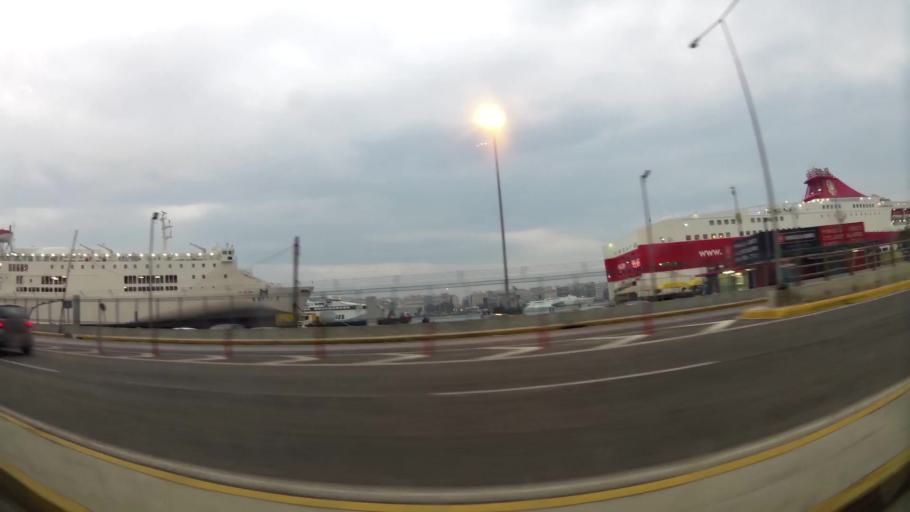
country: GR
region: Attica
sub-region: Nomos Attikis
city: Piraeus
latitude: 37.9456
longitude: 23.6354
